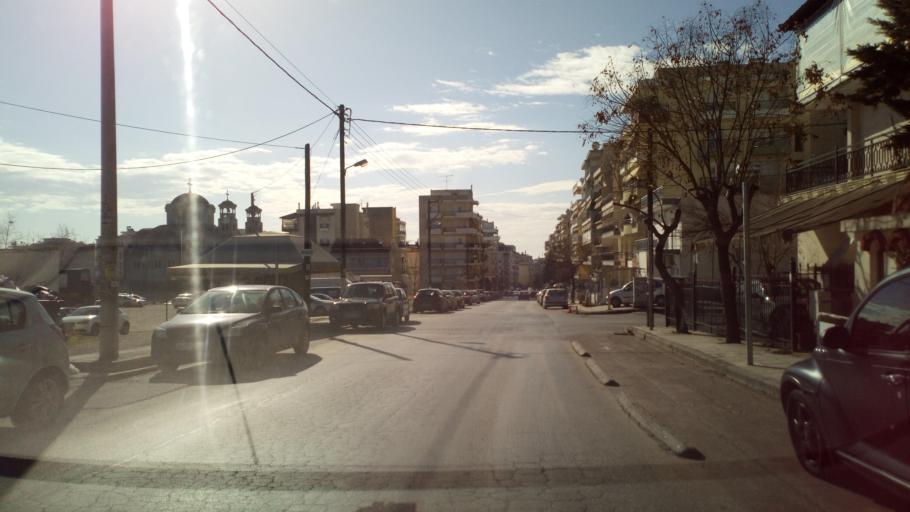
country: GR
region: Central Macedonia
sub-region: Nomos Thessalonikis
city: Evosmos
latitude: 40.6764
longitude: 22.9084
